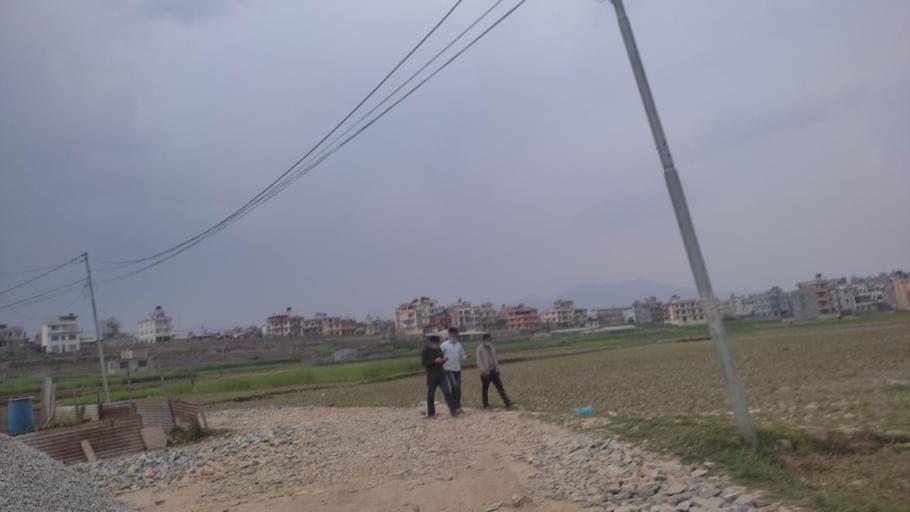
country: NP
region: Central Region
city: Kirtipur
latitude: 27.6630
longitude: 85.2747
